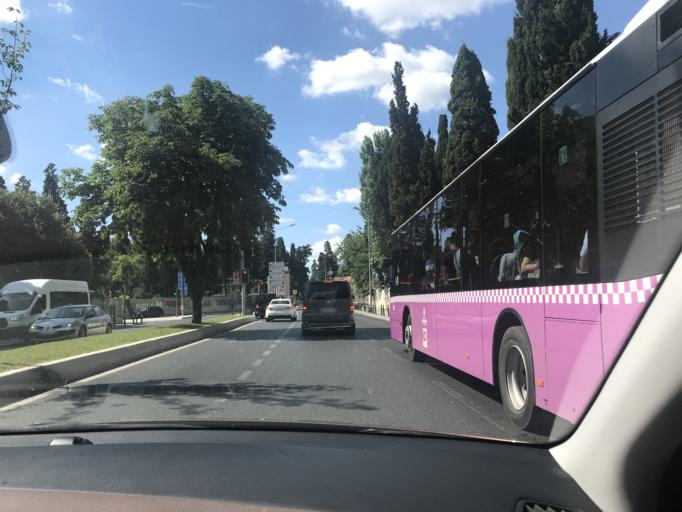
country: TR
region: Istanbul
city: UEskuedar
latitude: 41.0119
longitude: 29.0206
